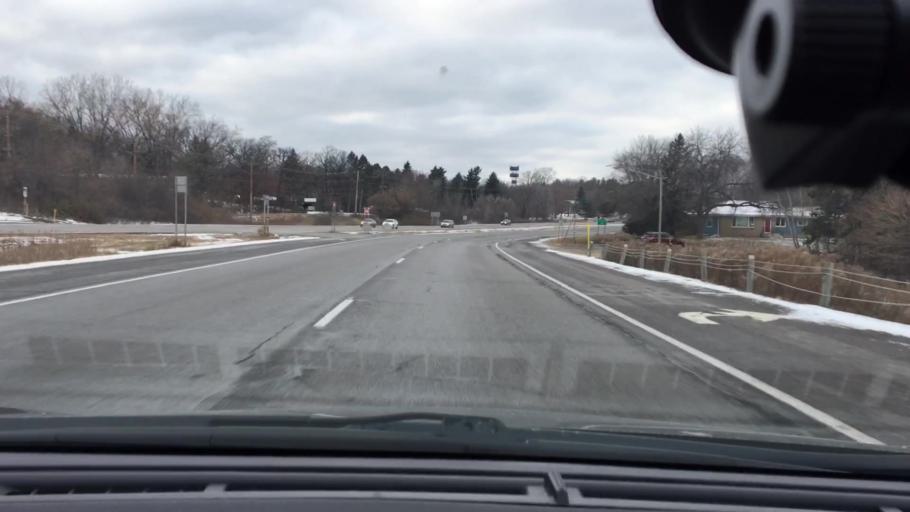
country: US
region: Minnesota
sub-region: Hennepin County
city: Plymouth
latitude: 44.9902
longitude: -93.4293
